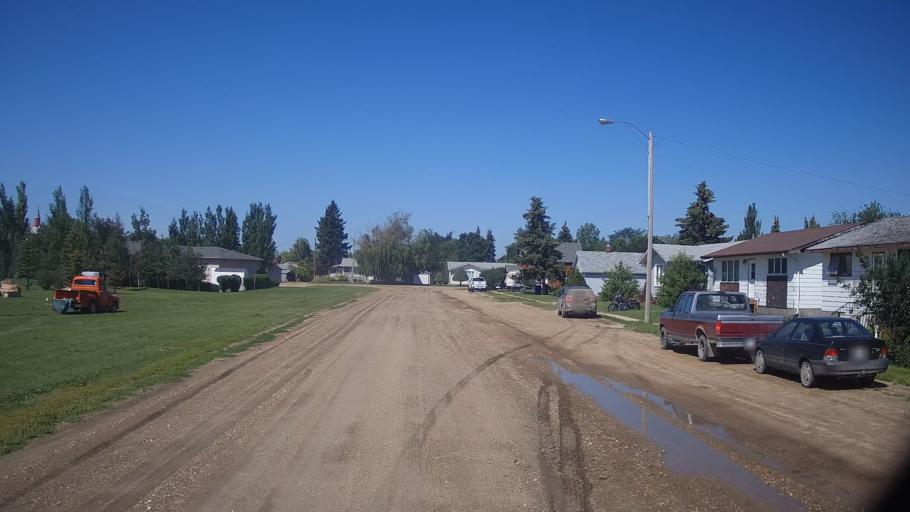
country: CA
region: Saskatchewan
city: Saskatoon
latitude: 51.8967
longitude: -106.0541
